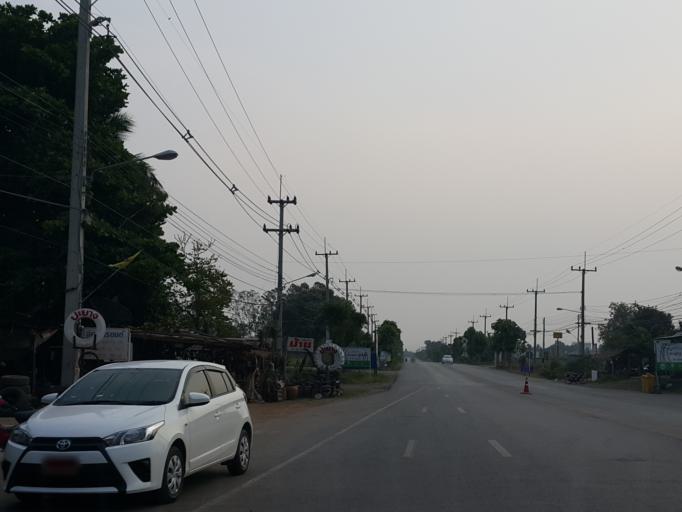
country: TH
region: Uthai Thani
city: Huai Khot
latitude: 15.1741
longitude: 99.6961
